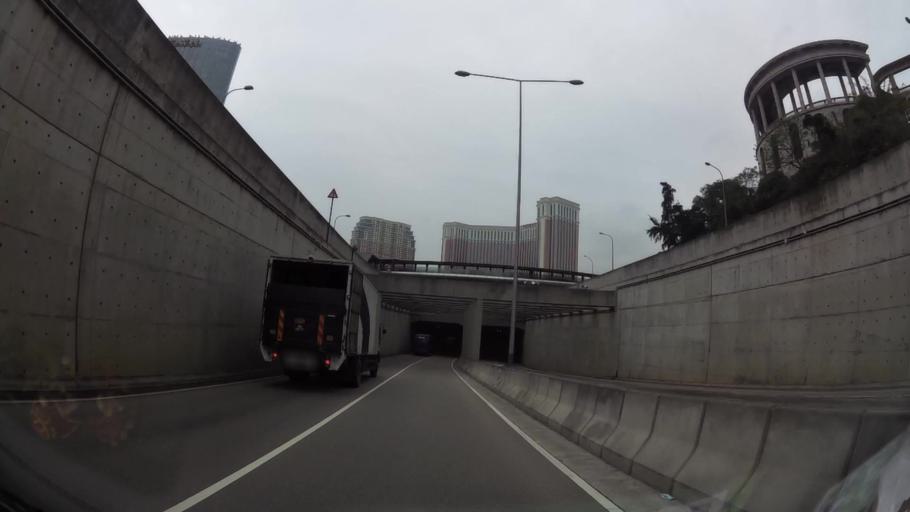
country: MO
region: Macau
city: Macau
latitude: 22.1520
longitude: 113.5649
